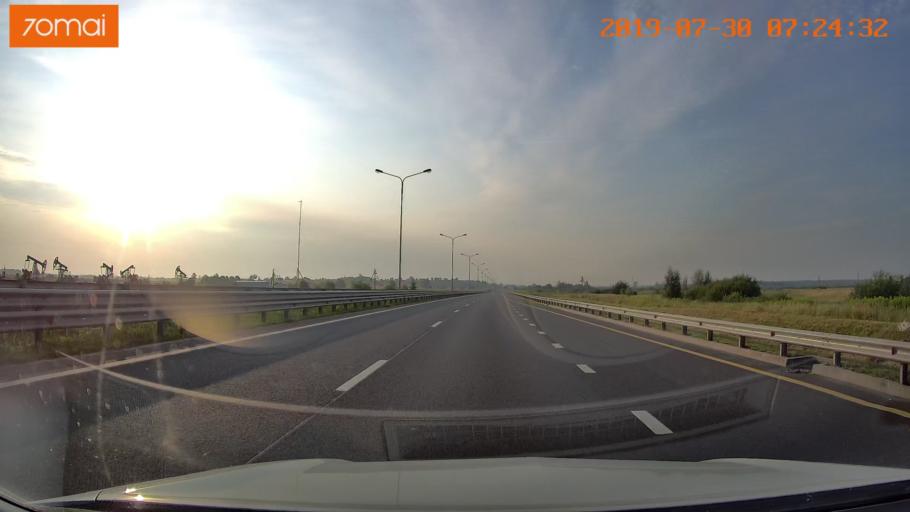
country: RU
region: Kaliningrad
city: Bol'shoe Isakovo
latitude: 54.6930
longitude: 20.8145
